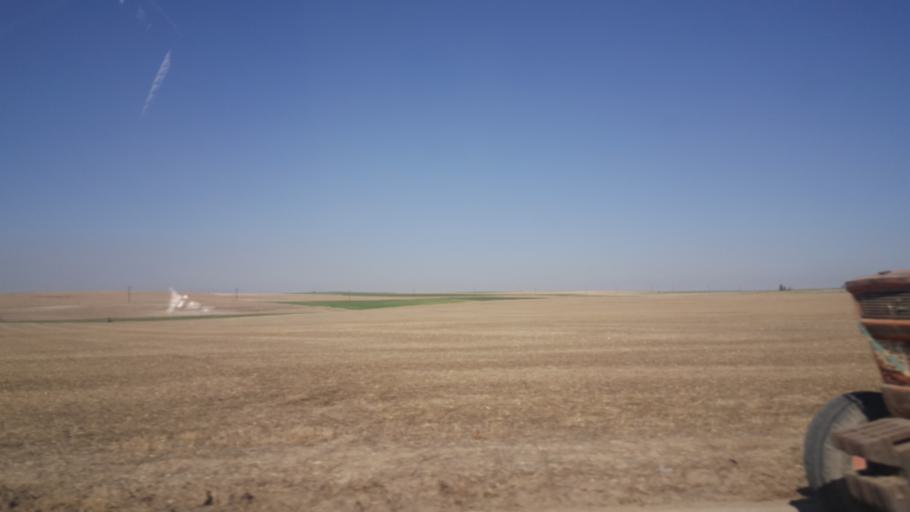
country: TR
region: Konya
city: Celtik
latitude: 39.0612
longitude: 31.8652
